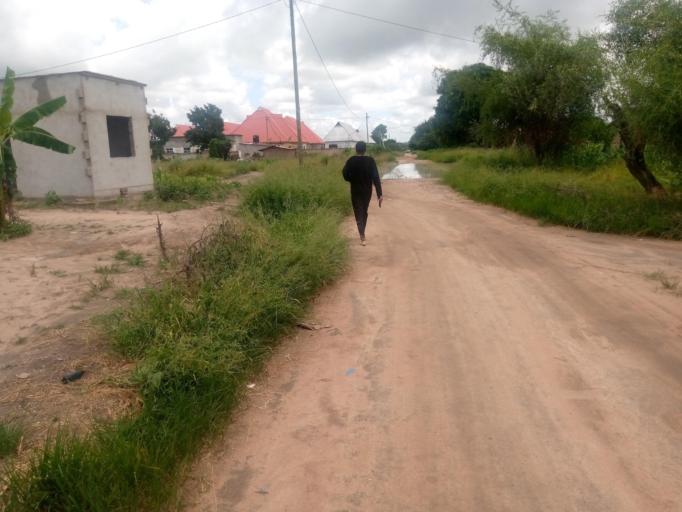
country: TZ
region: Dodoma
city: Dodoma
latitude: -6.1187
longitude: 35.7395
